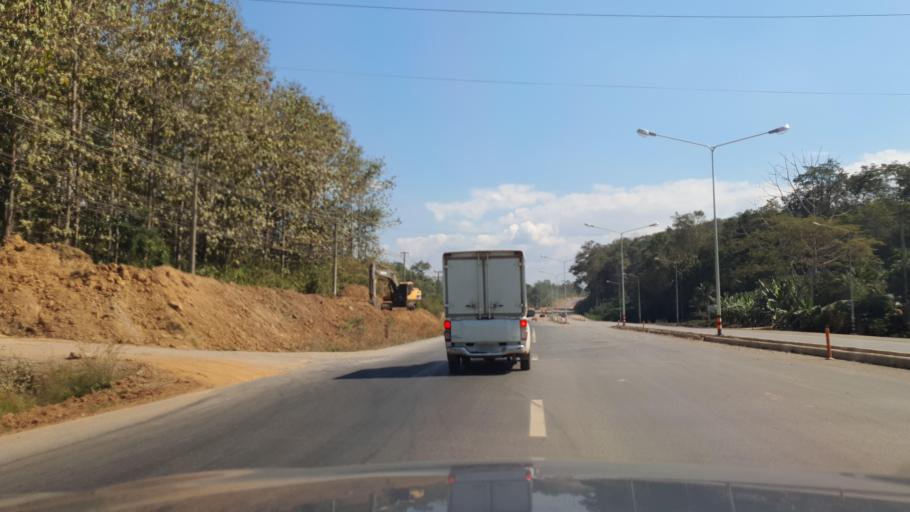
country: TH
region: Nan
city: Nan
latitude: 18.8295
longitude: 100.7559
